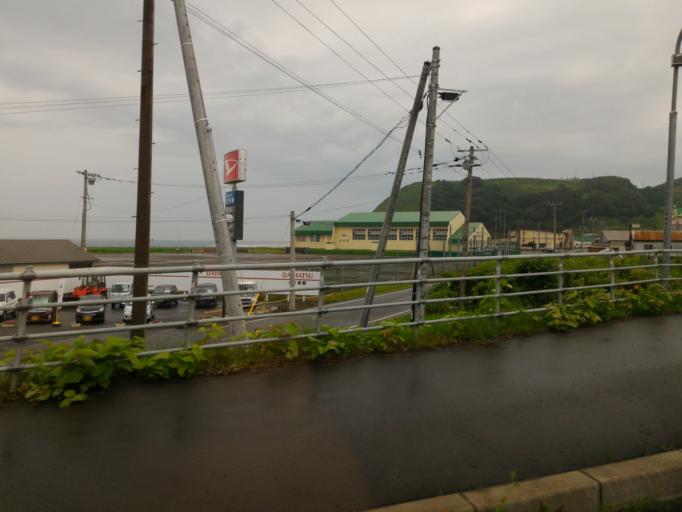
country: JP
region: Hokkaido
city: Rumoi
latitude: 44.0251
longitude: 141.6663
